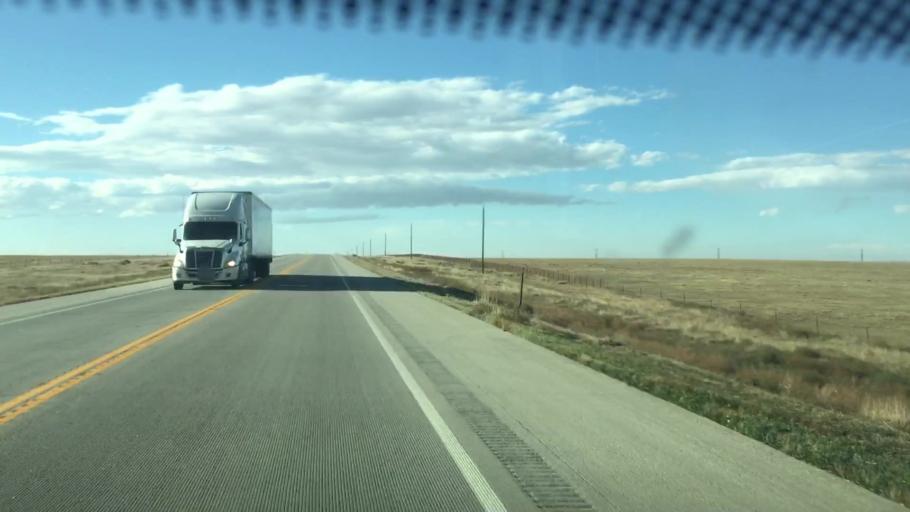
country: US
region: Colorado
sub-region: Lincoln County
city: Hugo
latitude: 39.0771
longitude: -103.3829
